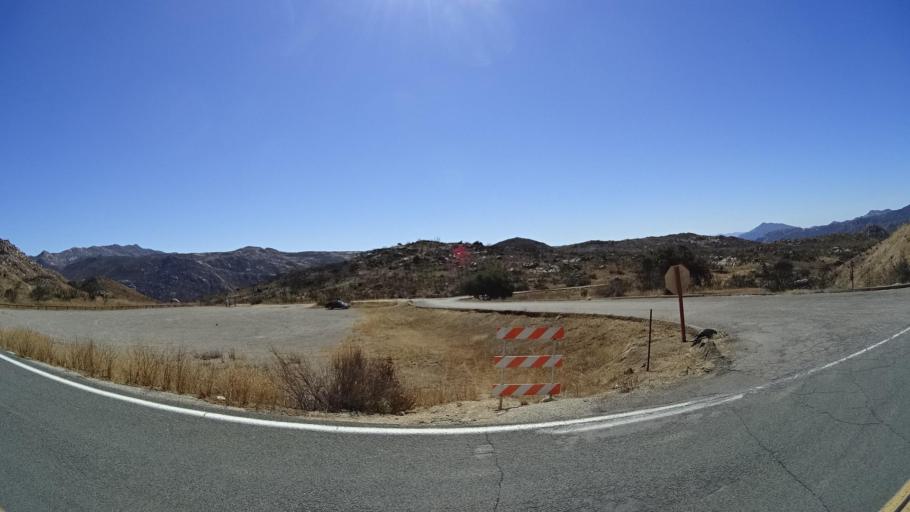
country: US
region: California
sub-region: San Diego County
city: Descanso
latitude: 32.7476
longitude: -116.6696
